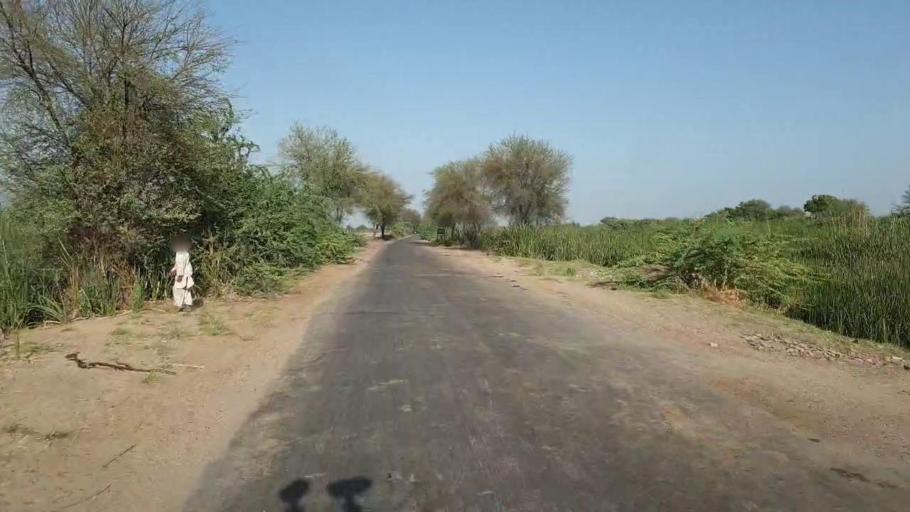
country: PK
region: Sindh
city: Nawabshah
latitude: 26.3728
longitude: 68.4712
